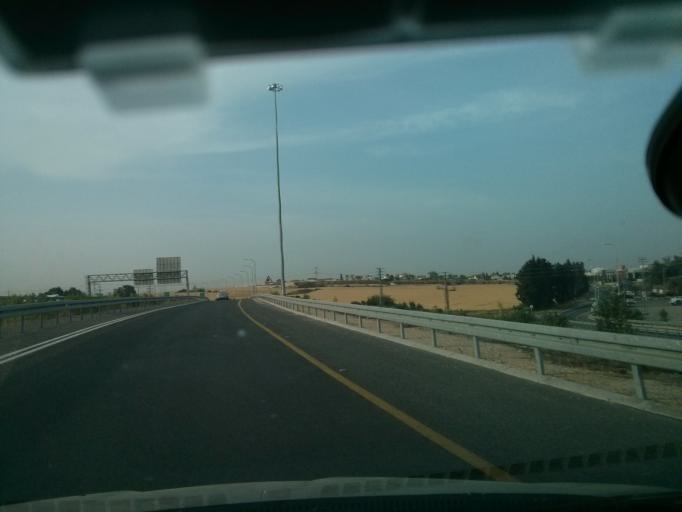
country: IL
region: Central District
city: Gedera
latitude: 31.8022
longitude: 34.7635
